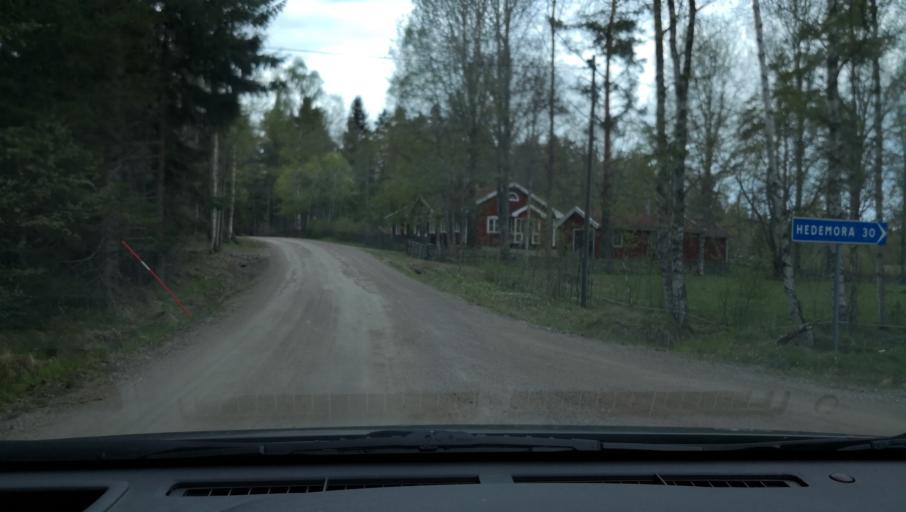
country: SE
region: Vaestmanland
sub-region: Fagersta Kommun
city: Fagersta
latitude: 60.1194
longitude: 15.7930
